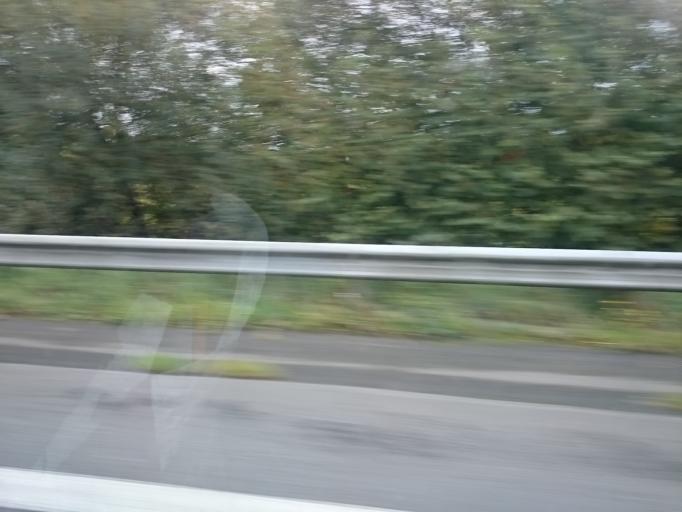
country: FR
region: Brittany
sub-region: Departement des Cotes-d'Armor
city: Plounevez-Moedec
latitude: 48.5622
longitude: -3.5162
